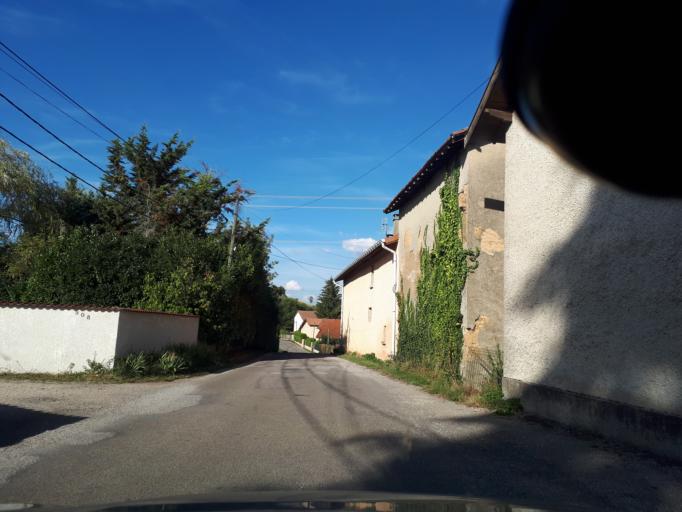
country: FR
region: Rhone-Alpes
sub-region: Departement de l'Isere
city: Chatonnay
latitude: 45.5122
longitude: 5.2299
